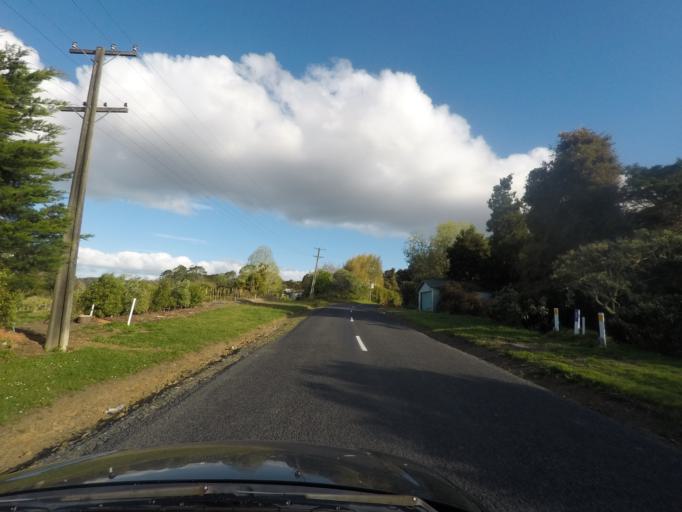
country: NZ
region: Auckland
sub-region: Auckland
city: Titirangi
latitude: -36.9244
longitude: 174.6186
